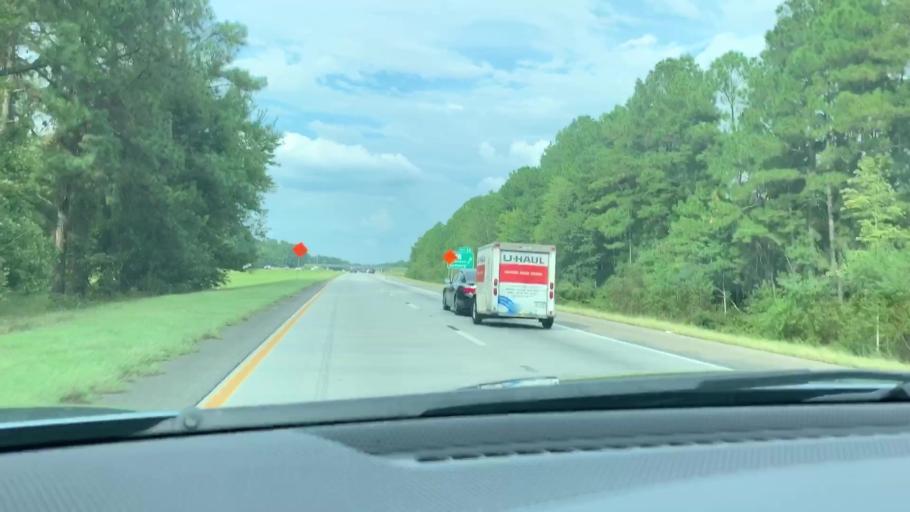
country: US
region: South Carolina
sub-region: Dorchester County
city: Saint George
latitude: 33.0775
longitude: -80.6560
